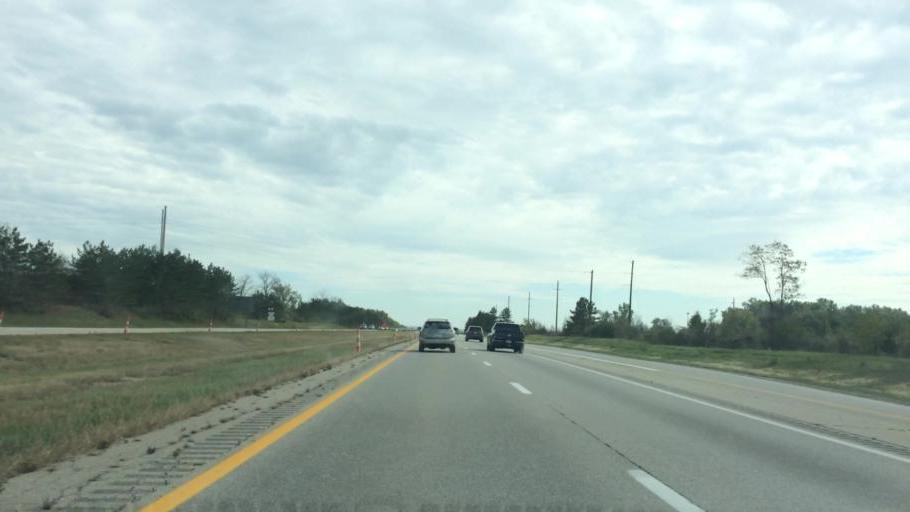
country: US
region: Ohio
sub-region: Union County
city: New California
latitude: 40.1589
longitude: -83.2291
